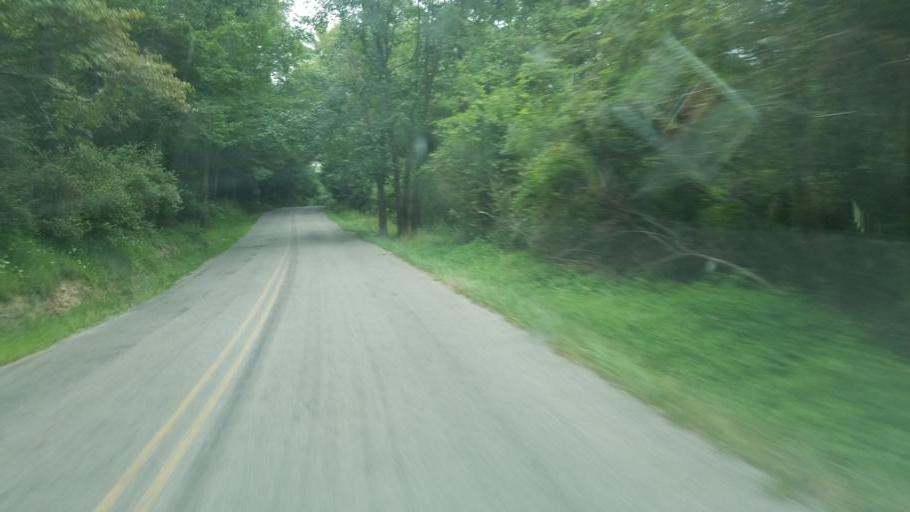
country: US
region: Pennsylvania
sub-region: Clarion County
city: Marianne
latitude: 41.1809
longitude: -79.4639
